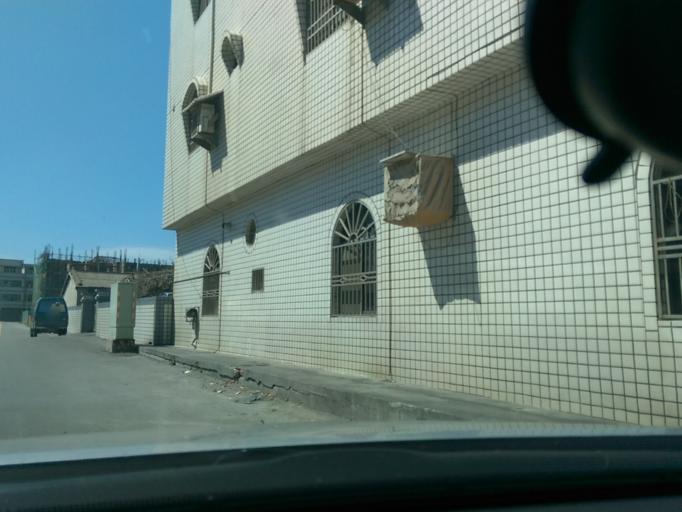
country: TW
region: Taiwan
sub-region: Yunlin
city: Douliu
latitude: 23.7475
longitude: 120.2523
